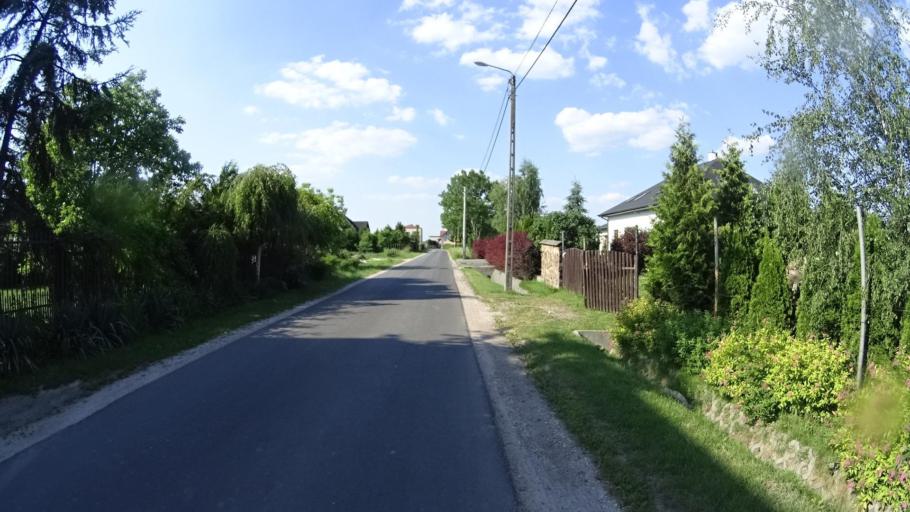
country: PL
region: Masovian Voivodeship
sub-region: Powiat warszawski zachodni
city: Ozarow Mazowiecki
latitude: 52.2119
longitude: 20.7580
